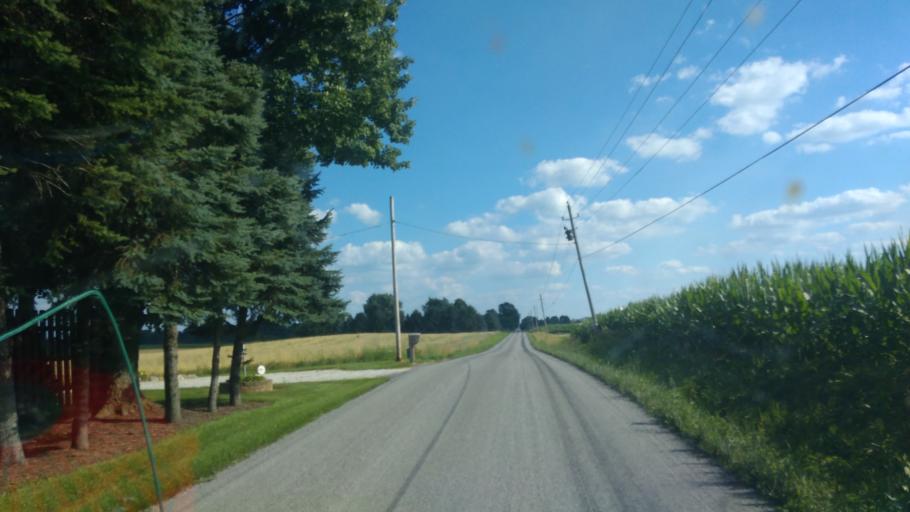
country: US
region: Ohio
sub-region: Wayne County
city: Apple Creek
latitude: 40.7157
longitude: -81.9060
